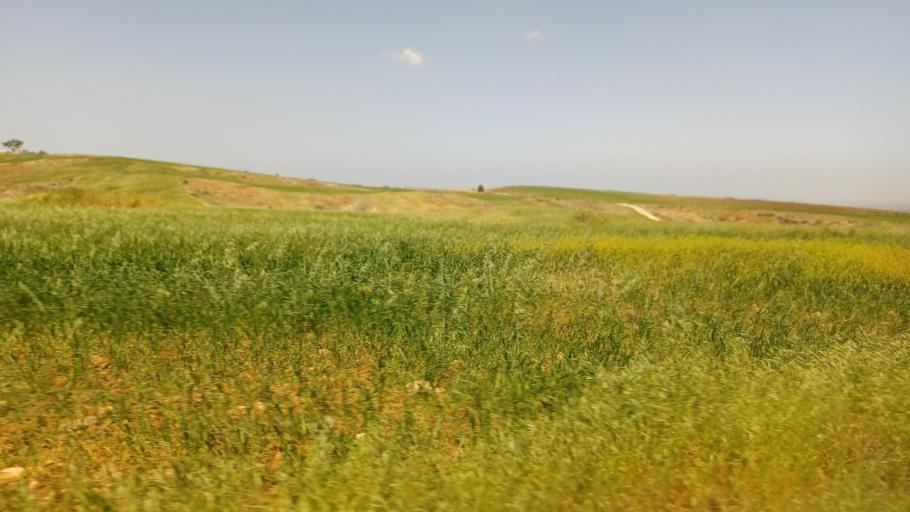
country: CY
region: Lefkosia
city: Lefka
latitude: 35.0930
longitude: 32.9316
